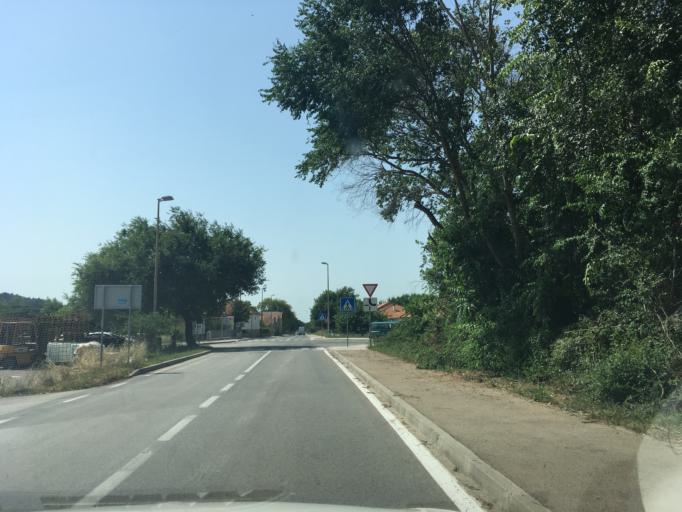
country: HR
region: Zadarska
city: Benkovac
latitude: 44.0277
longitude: 15.6135
